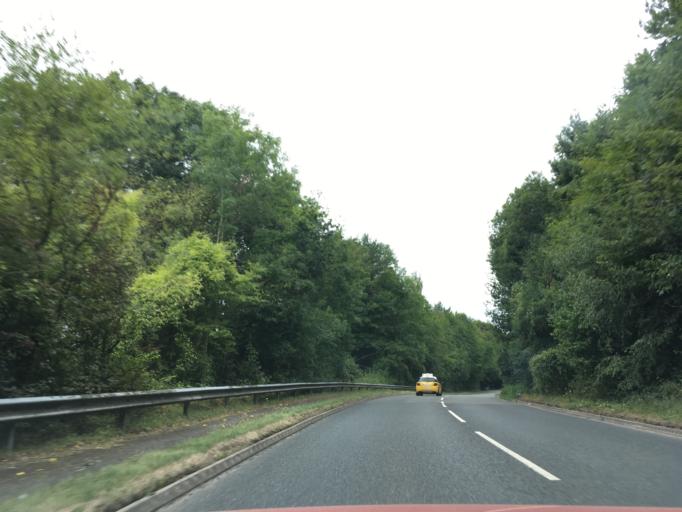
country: GB
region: Wales
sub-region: Monmouthshire
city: Gilwern
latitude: 51.8363
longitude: -3.0767
